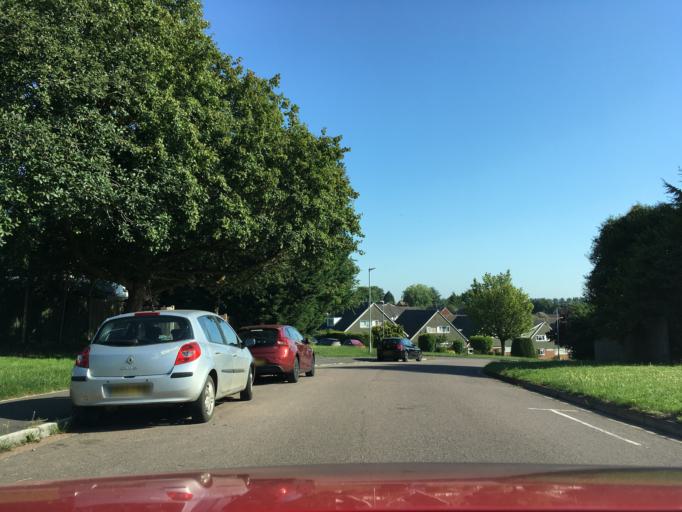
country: GB
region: England
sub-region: South Gloucestershire
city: Pucklechurch
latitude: 51.4828
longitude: -2.4335
